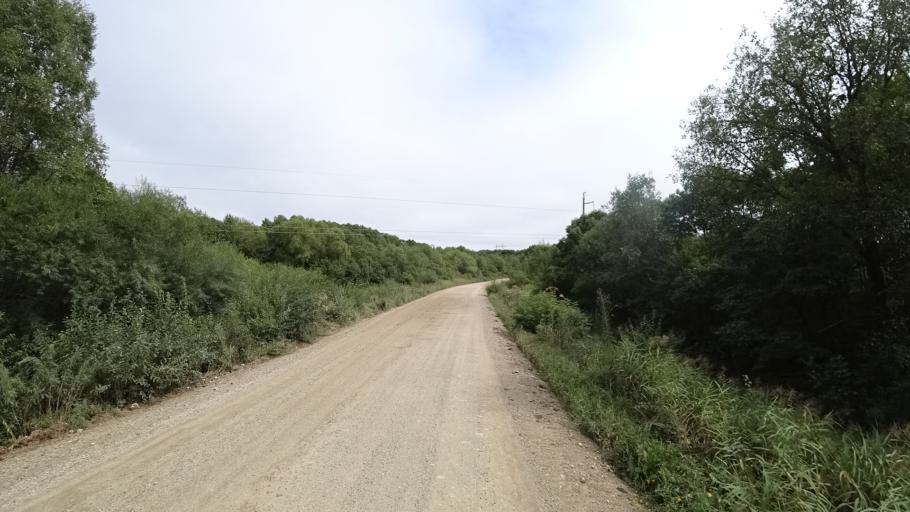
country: RU
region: Primorskiy
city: Lyalichi
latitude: 44.0994
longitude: 132.4263
